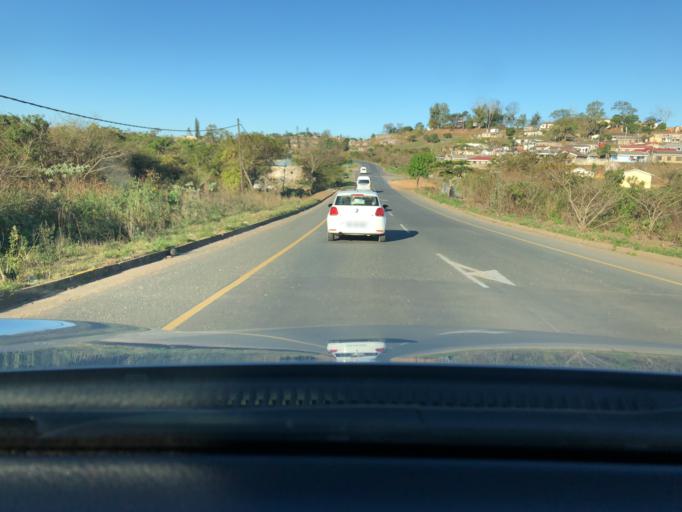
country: ZA
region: KwaZulu-Natal
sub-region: eThekwini Metropolitan Municipality
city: Umkomaas
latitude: -30.0358
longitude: 30.8175
